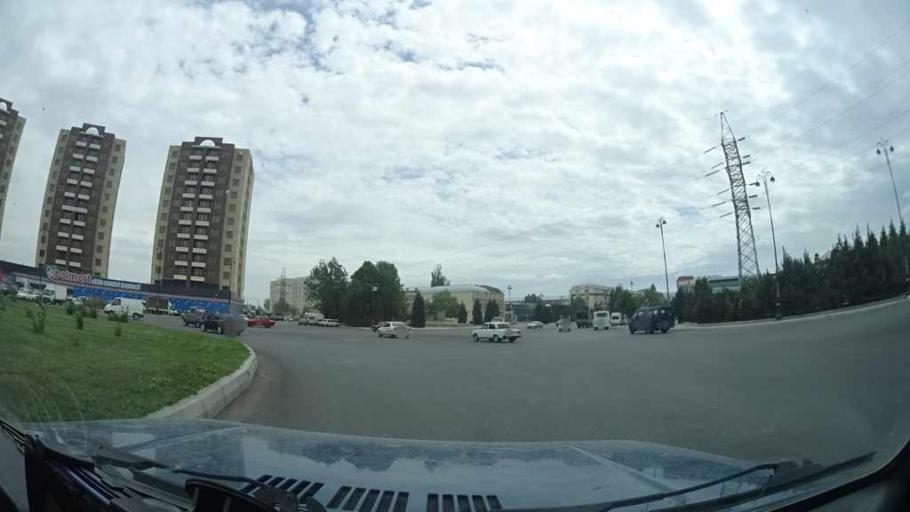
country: AZ
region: Ganja City
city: Ganja
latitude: 40.6972
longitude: 46.3724
